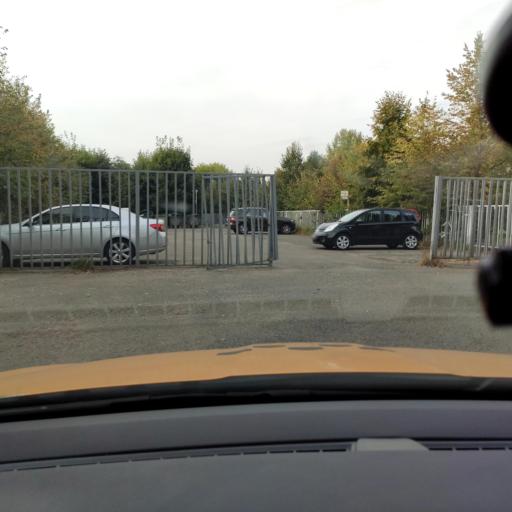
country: RU
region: Moscow
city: Shchukino
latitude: 55.7648
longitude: 37.4395
